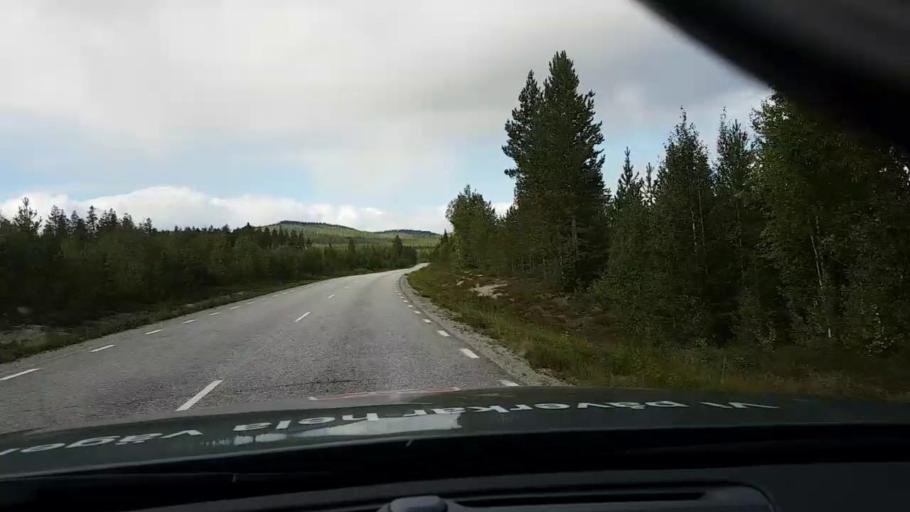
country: SE
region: Vaesternorrland
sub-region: OErnskoeldsviks Kommun
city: Bredbyn
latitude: 63.6800
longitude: 17.7865
